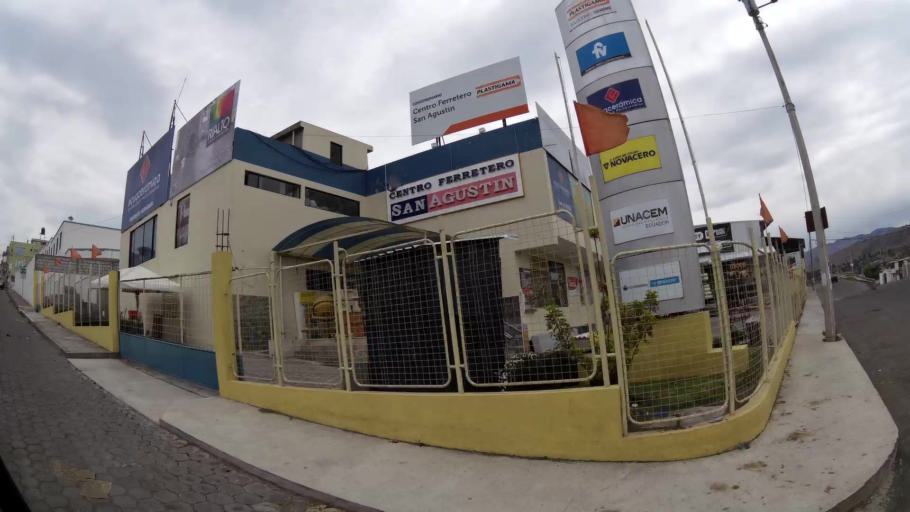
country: EC
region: Cotopaxi
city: Latacunga
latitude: -0.9593
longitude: -78.6117
